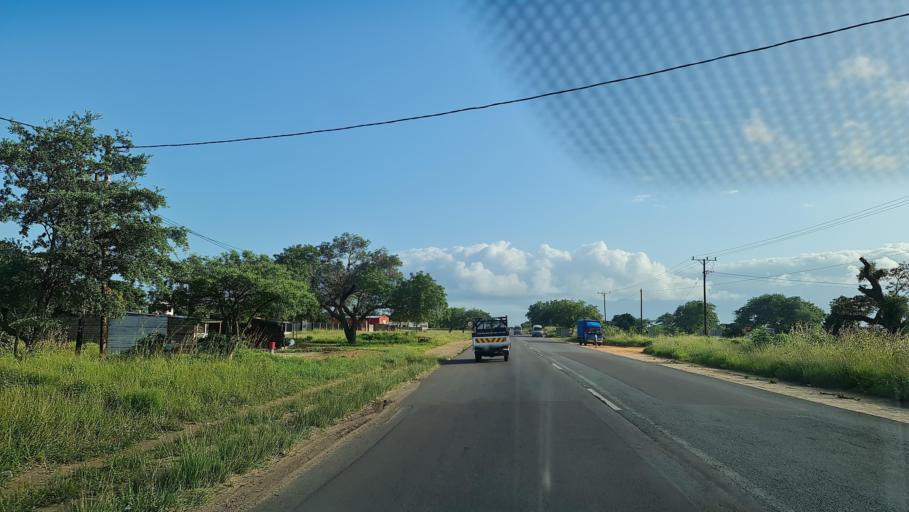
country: MZ
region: Maputo City
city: Maputo
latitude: -25.6879
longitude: 32.6647
